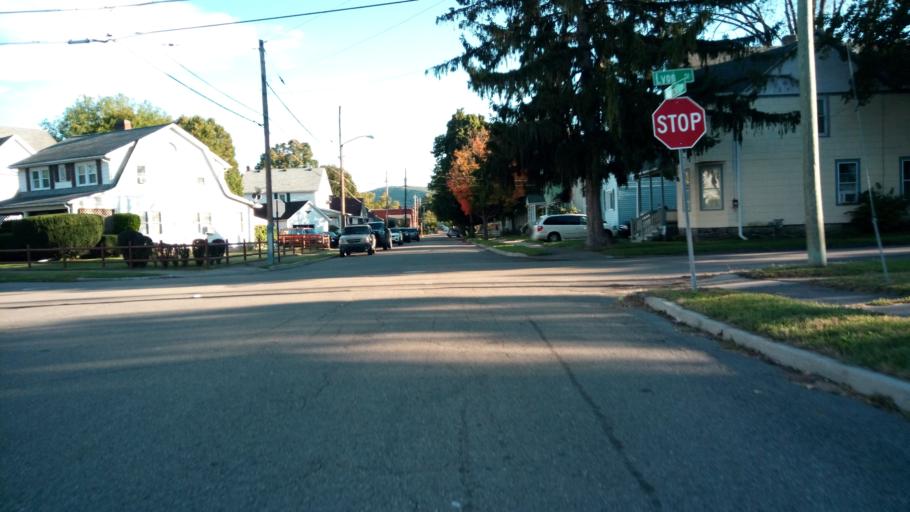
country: US
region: New York
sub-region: Chemung County
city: Elmira
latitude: 42.0729
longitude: -76.8069
